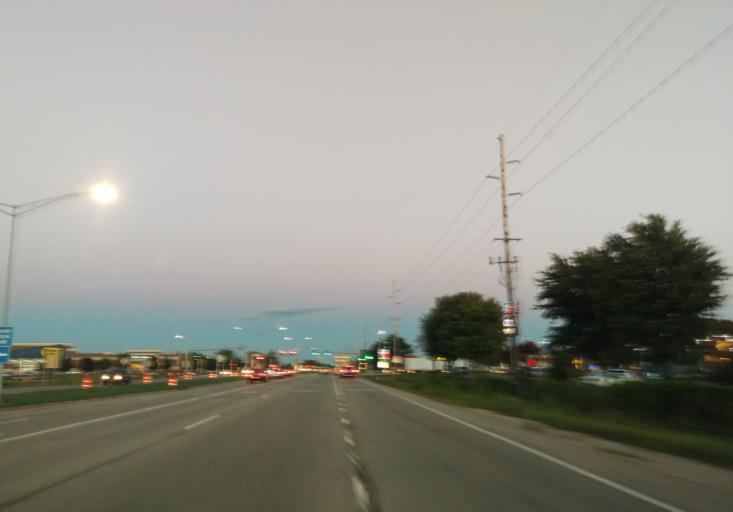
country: US
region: Wisconsin
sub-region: Rock County
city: Janesville
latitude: 42.7159
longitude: -88.9818
